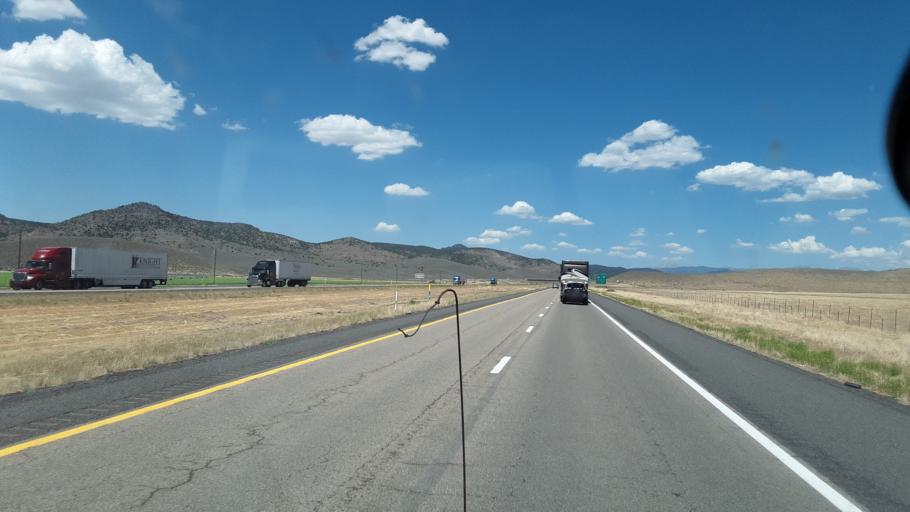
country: US
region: Utah
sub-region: Beaver County
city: Beaver
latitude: 38.0608
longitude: -112.6958
